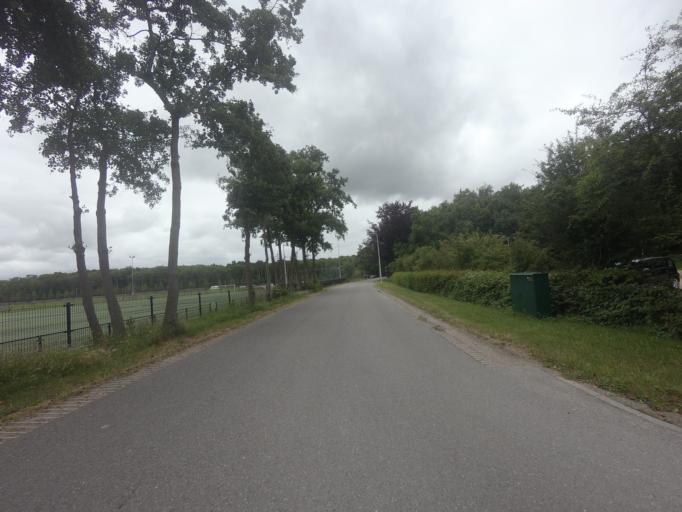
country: NL
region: North Holland
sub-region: Gemeente Bloemendaal
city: Bloemendaal
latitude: 52.4150
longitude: 4.6141
